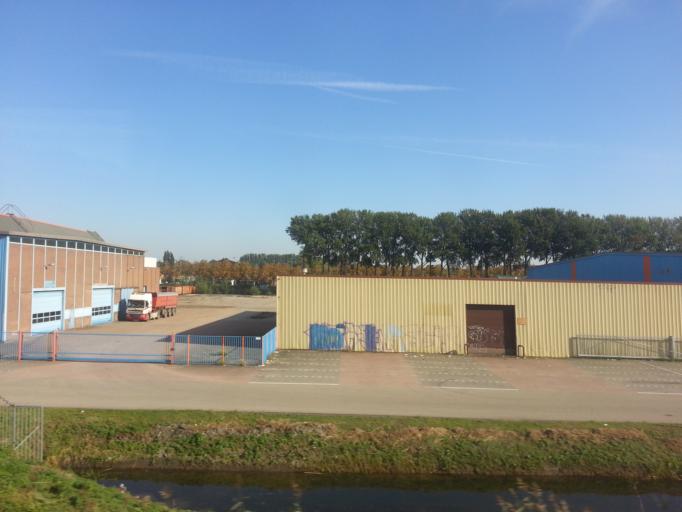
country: NL
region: Utrecht
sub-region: Stichtse Vecht
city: Maarssen
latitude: 52.1181
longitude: 5.0642
